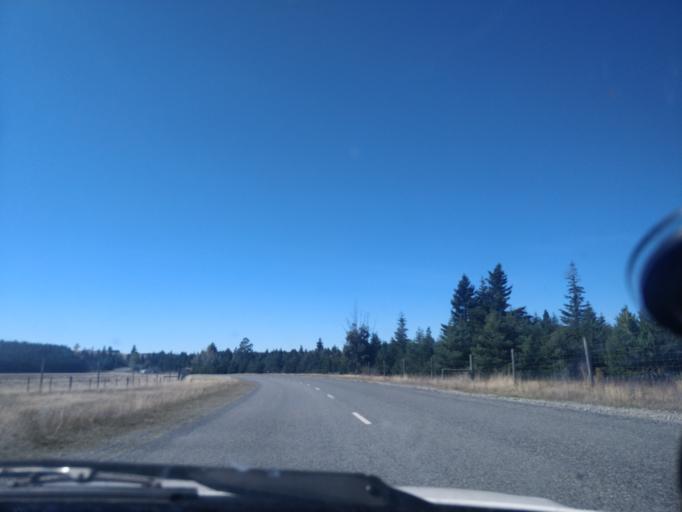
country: NZ
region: Otago
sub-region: Queenstown-Lakes District
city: Wanaka
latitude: -44.2722
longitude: 170.0584
